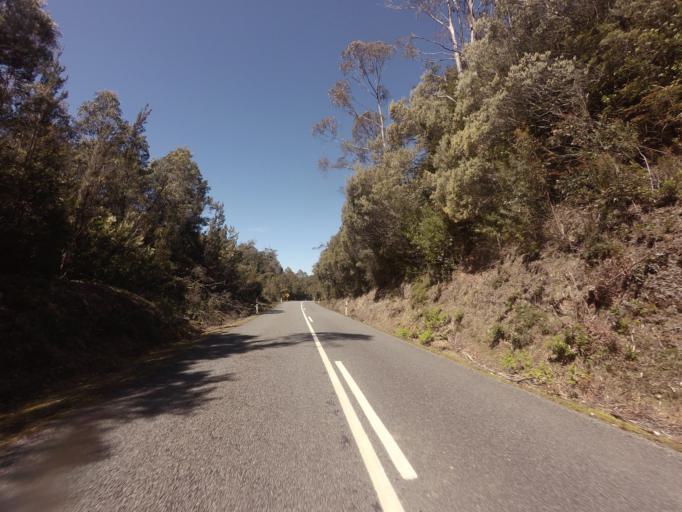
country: AU
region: Tasmania
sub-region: Huon Valley
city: Geeveston
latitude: -42.8166
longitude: 146.3637
